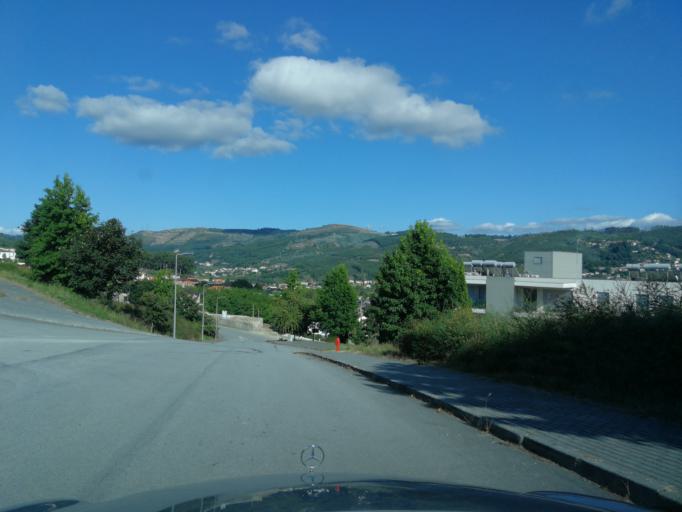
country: PT
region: Braga
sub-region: Braga
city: Adaufe
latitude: 41.5715
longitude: -8.3856
